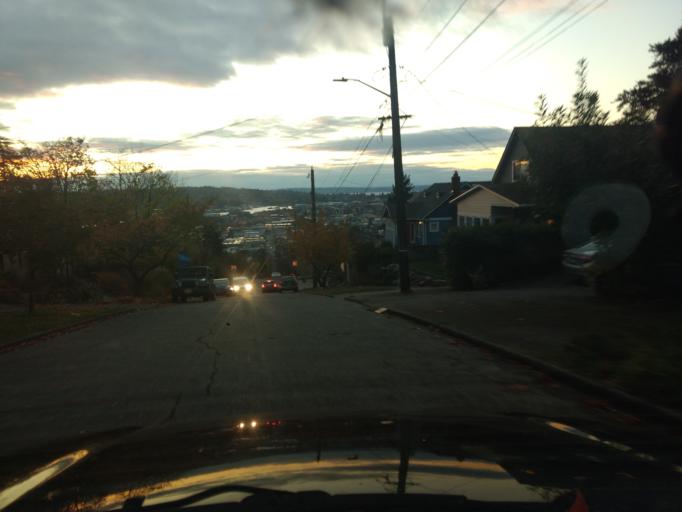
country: US
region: Washington
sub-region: King County
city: Seattle
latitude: 47.6643
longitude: -122.3576
